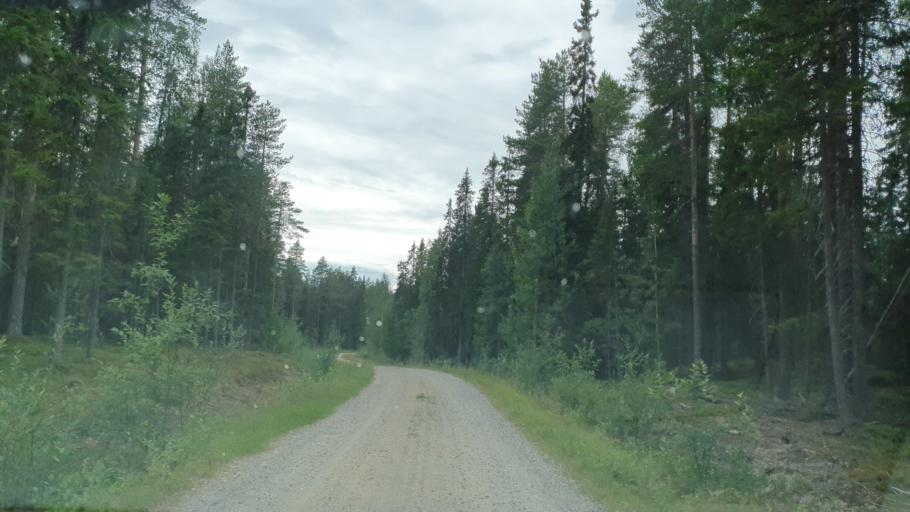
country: FI
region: Kainuu
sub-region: Kehys-Kainuu
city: Kuhmo
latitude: 64.2027
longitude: 29.3847
